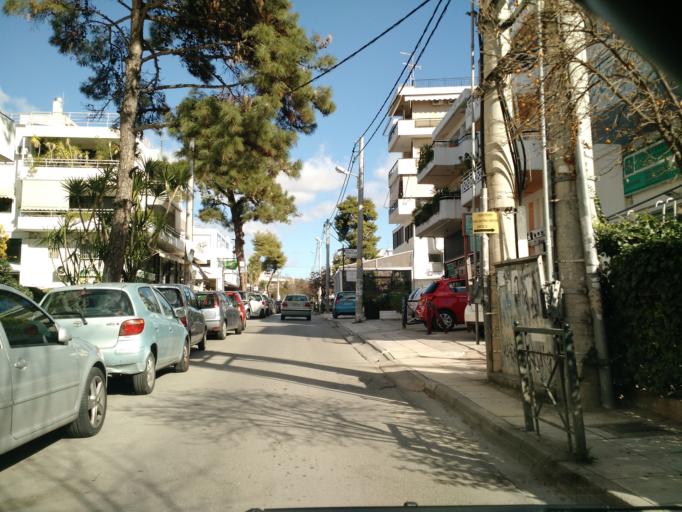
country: GR
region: Attica
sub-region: Nomarchia Athinas
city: Agia Paraskevi
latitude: 38.0057
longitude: 23.8265
